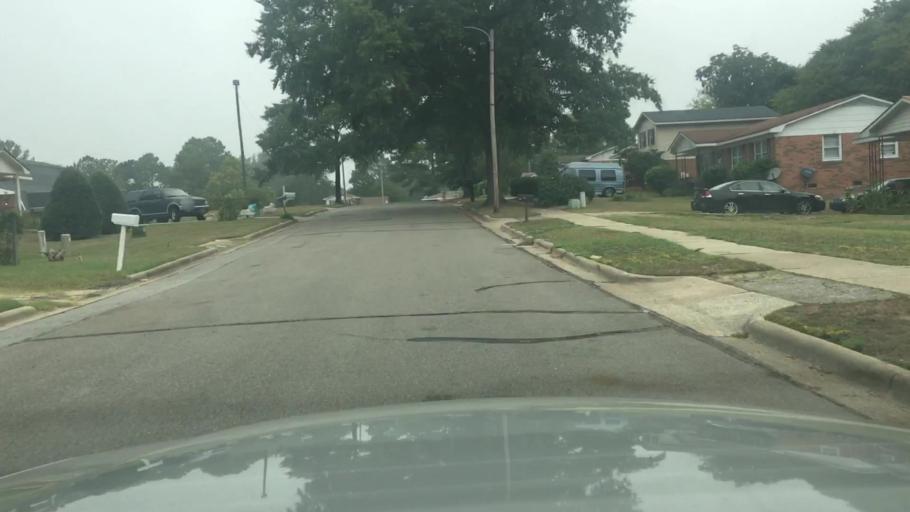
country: US
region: North Carolina
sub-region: Cumberland County
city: Fayetteville
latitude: 35.0692
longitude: -78.8859
